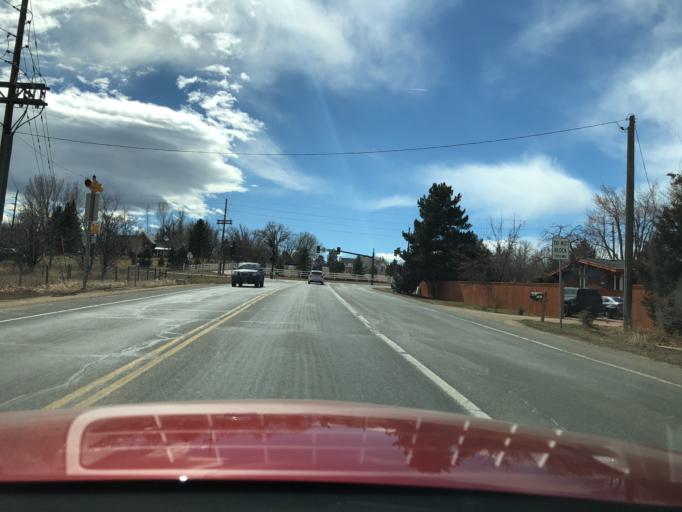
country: US
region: Colorado
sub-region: Boulder County
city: Superior
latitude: 40.0011
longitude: -105.1782
